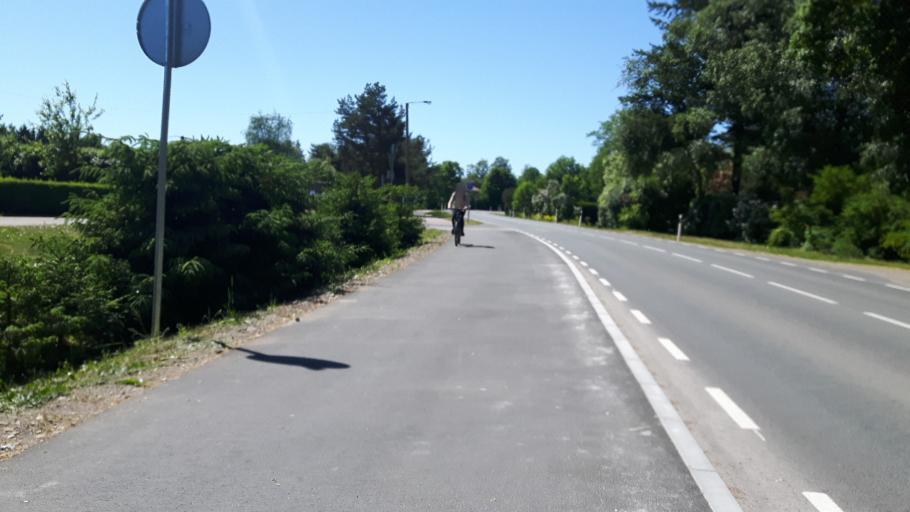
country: EE
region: Harju
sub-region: Kuusalu vald
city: Kuusalu
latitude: 59.4547
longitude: 25.4404
